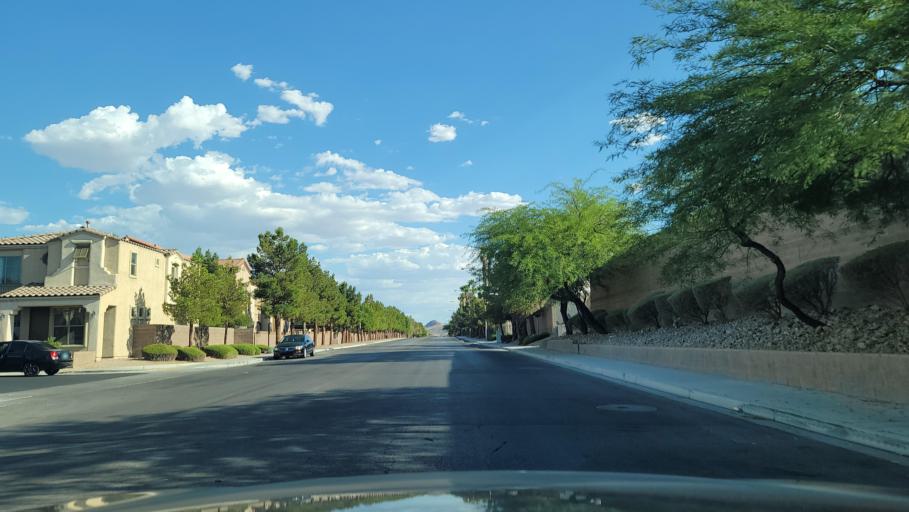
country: US
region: Nevada
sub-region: Clark County
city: Summerlin South
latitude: 36.0986
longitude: -115.3019
